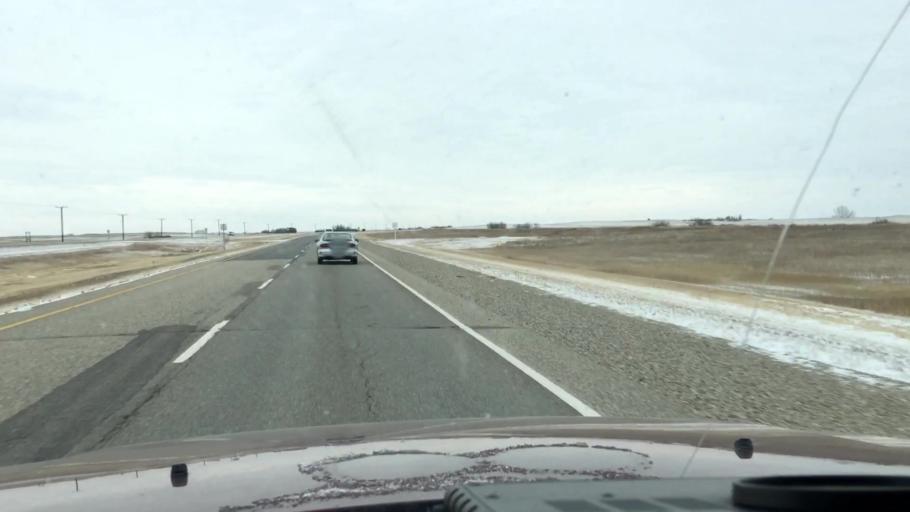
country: CA
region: Saskatchewan
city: Watrous
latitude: 51.4404
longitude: -106.2088
